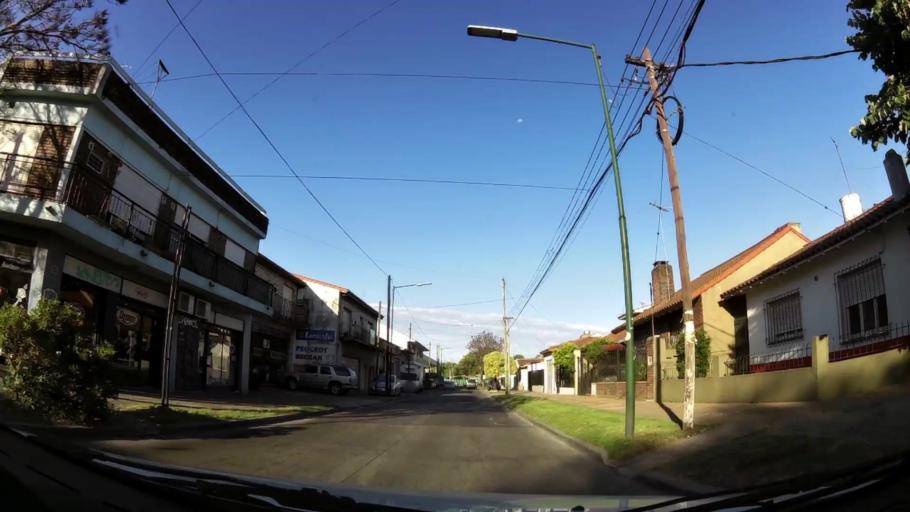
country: AR
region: Buenos Aires
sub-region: Partido de San Isidro
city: San Isidro
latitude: -34.4686
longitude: -58.5430
